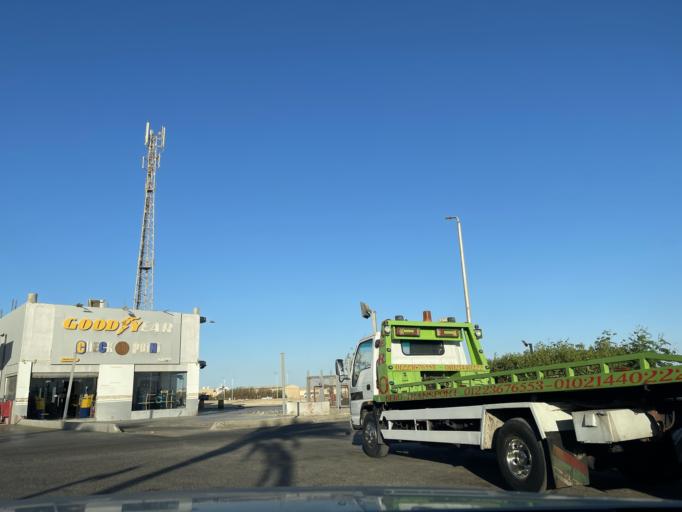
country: EG
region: Red Sea
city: Hurghada
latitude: 27.2328
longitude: 33.7812
